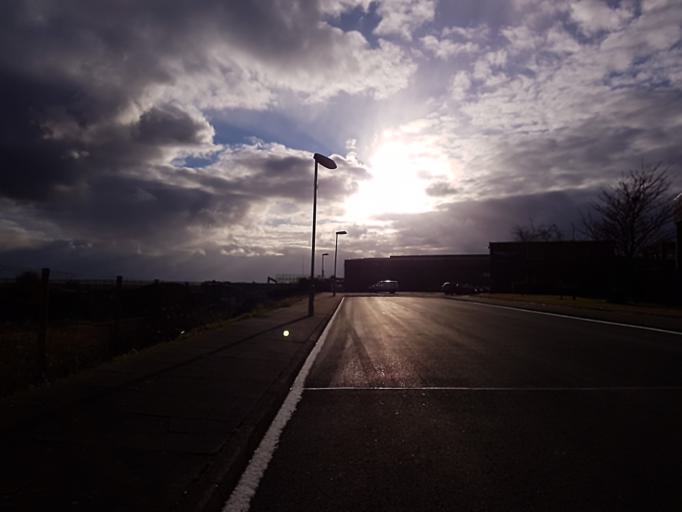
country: GB
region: England
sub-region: North East Lincolnshire
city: Grimsby
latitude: 53.5778
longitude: -0.0565
